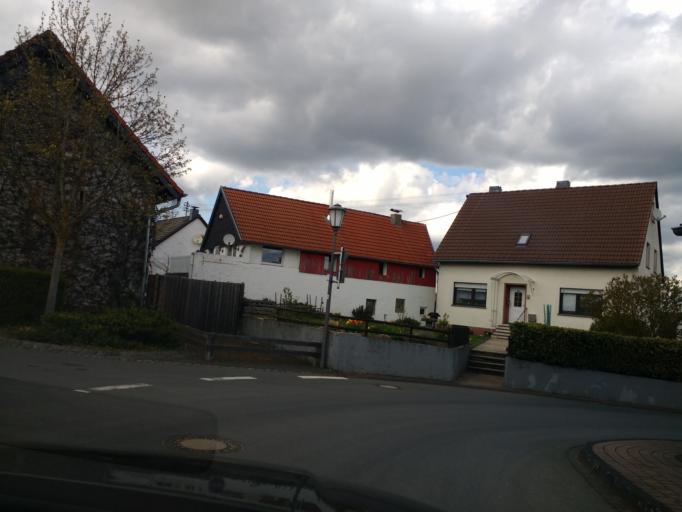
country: DE
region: Rheinland-Pfalz
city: Uxheim
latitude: 50.3424
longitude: 6.7436
